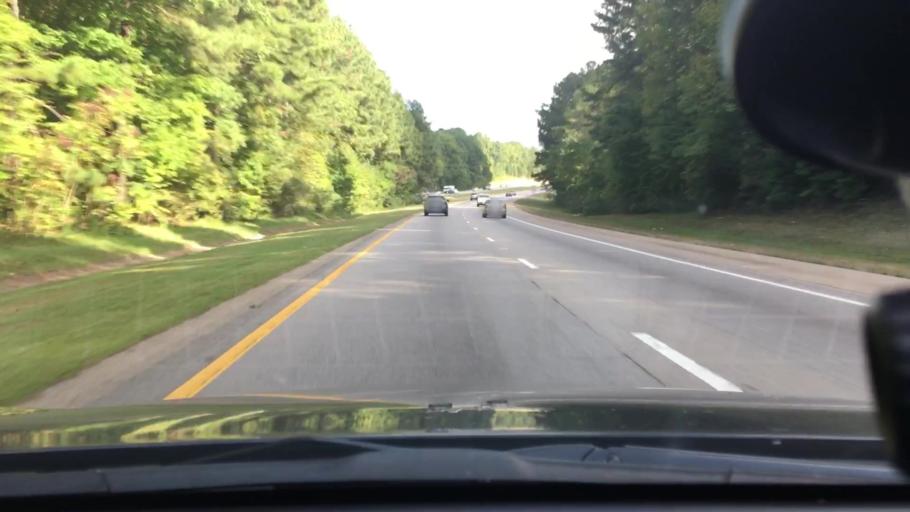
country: US
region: North Carolina
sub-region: Wake County
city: Cary
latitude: 35.8143
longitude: -78.7352
